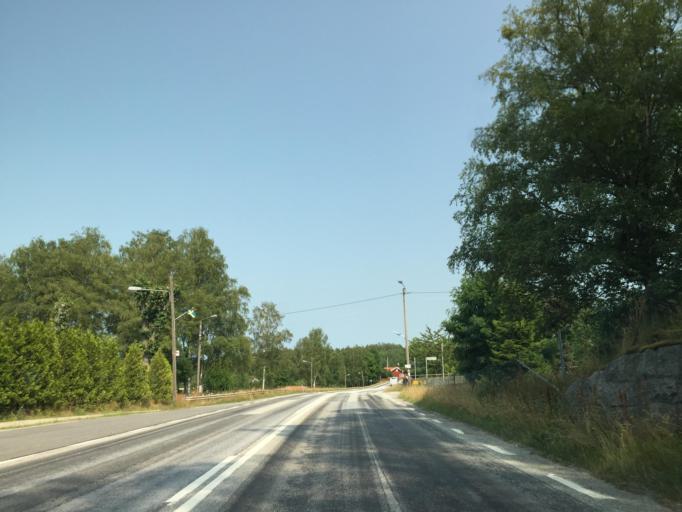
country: SE
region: Vaestra Goetaland
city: Svanesund
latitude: 58.0897
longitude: 11.9646
